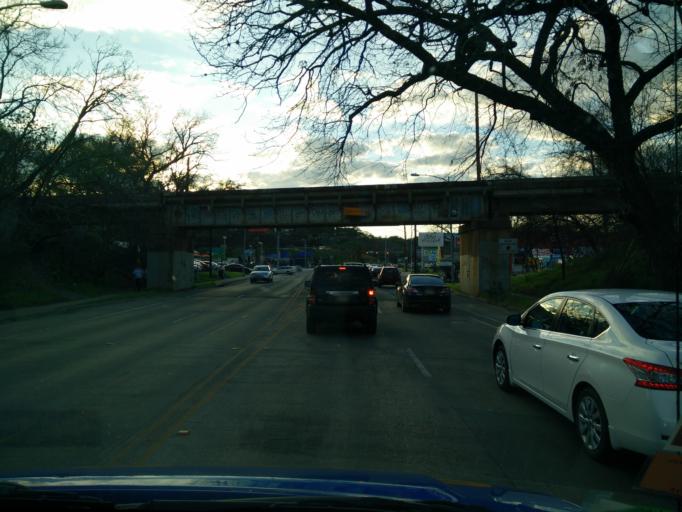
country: US
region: Texas
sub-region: Travis County
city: Austin
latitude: 30.2605
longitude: -97.7568
